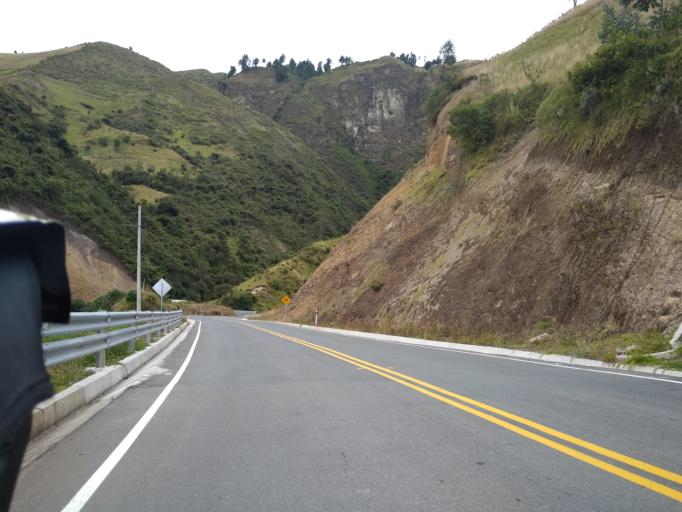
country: EC
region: Cotopaxi
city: Saquisili
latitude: -0.7565
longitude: -78.9136
